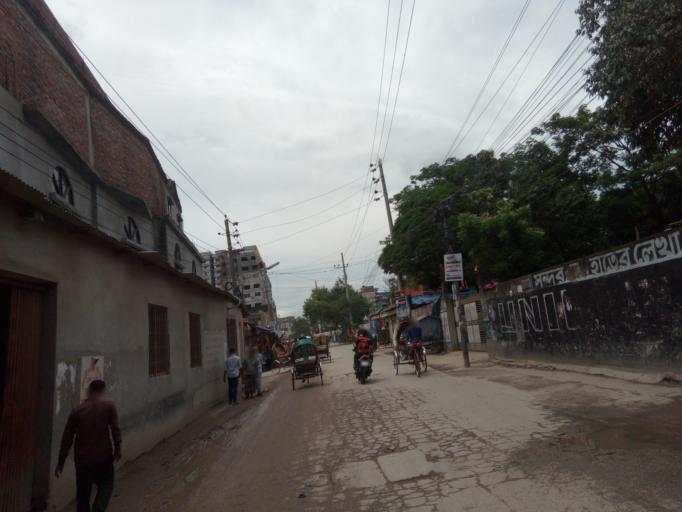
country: BD
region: Dhaka
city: Azimpur
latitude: 23.7610
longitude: 90.3589
